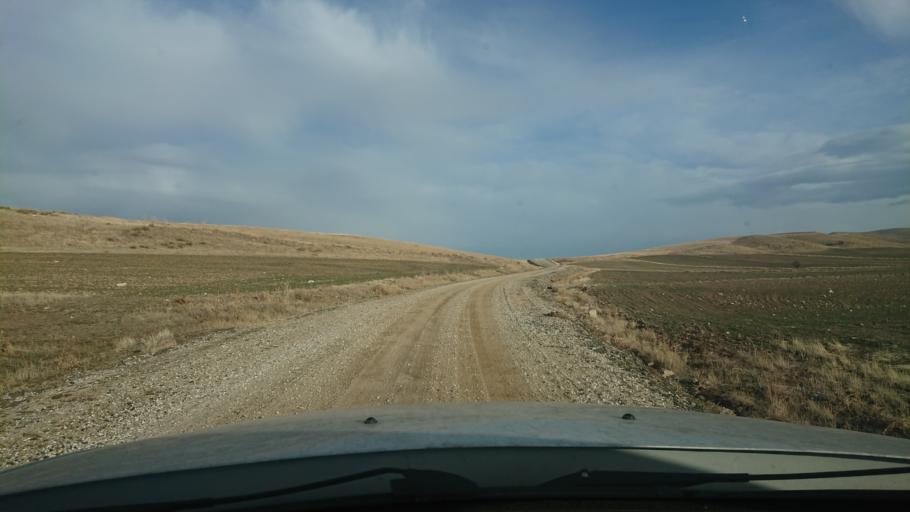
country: TR
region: Aksaray
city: Acipinar
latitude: 38.6858
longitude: 33.8696
